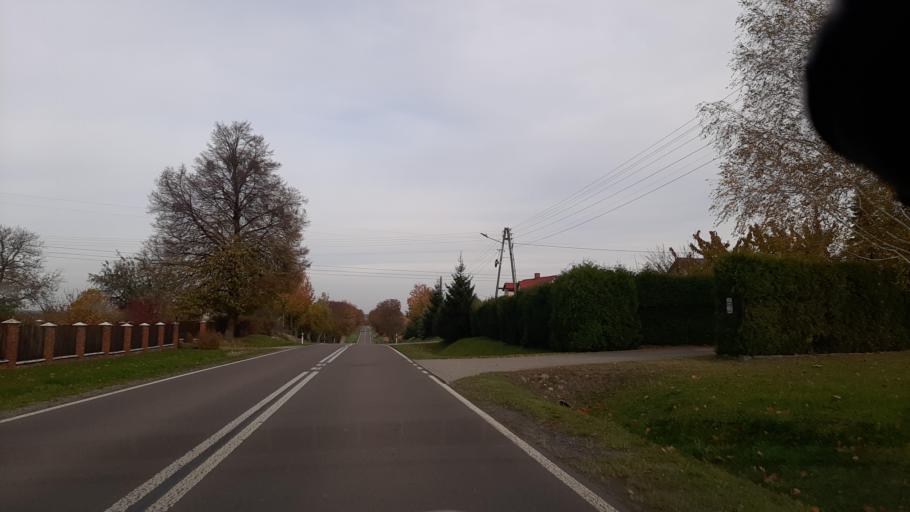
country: PL
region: Lublin Voivodeship
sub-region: Powiat pulawski
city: Markuszow
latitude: 51.3484
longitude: 22.2679
